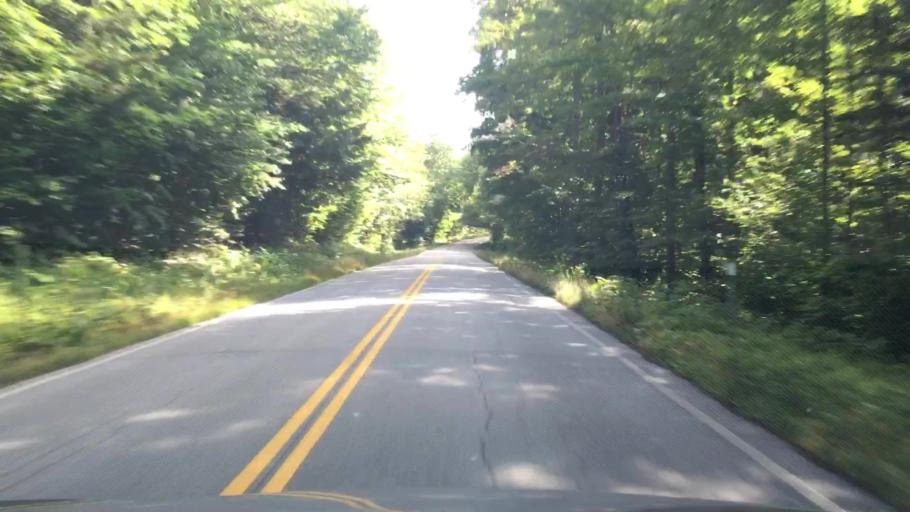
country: US
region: New Hampshire
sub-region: Carroll County
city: Tamworth
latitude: 44.0135
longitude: -71.3208
